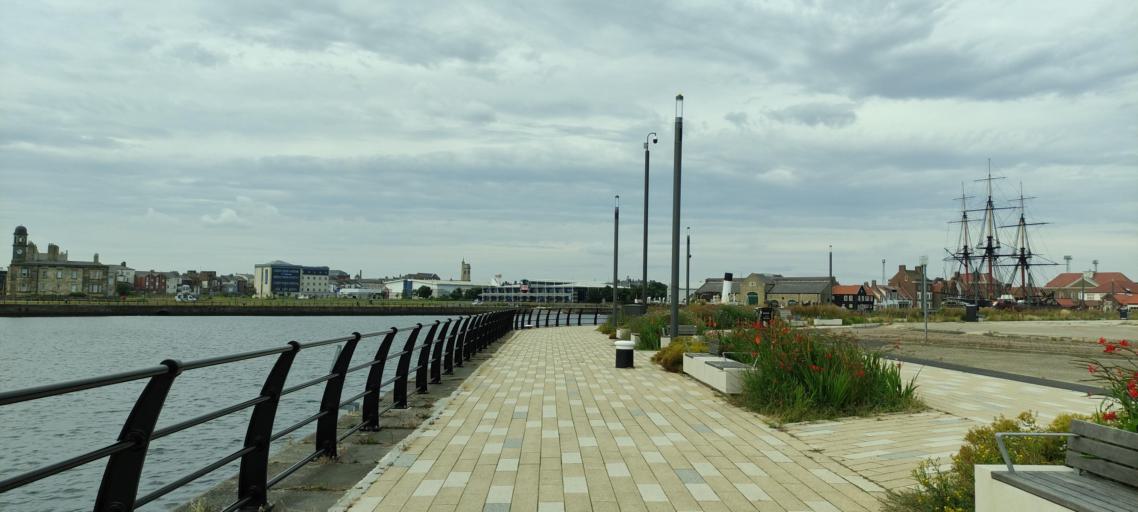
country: GB
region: England
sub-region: Hartlepool
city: Hartlepool
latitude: 54.6913
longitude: -1.2026
